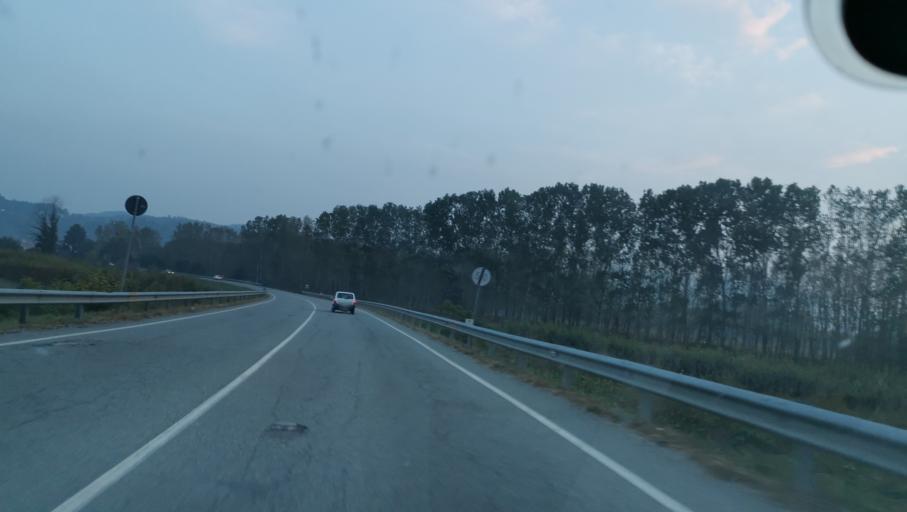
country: IT
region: Piedmont
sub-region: Provincia di Torino
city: Castiglione Torinese
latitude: 45.1286
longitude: 7.7849
